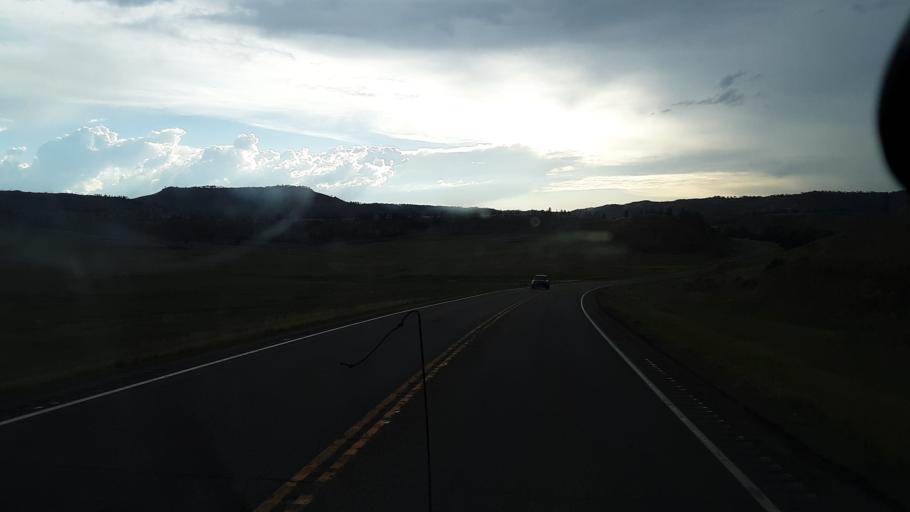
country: US
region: Montana
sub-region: Rosebud County
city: Lame Deer
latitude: 45.6147
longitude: -106.3793
